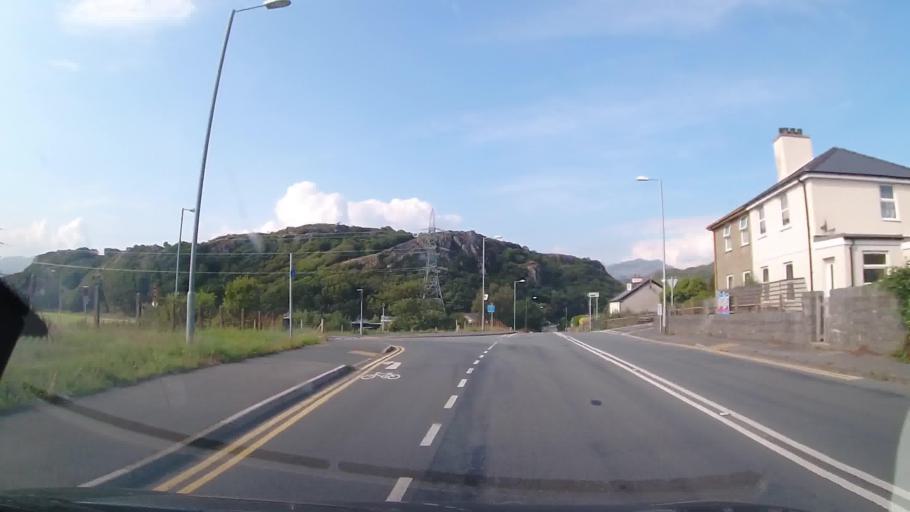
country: GB
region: Wales
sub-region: Gwynedd
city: Penrhyndeudraeth
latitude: 52.9182
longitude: -4.0518
